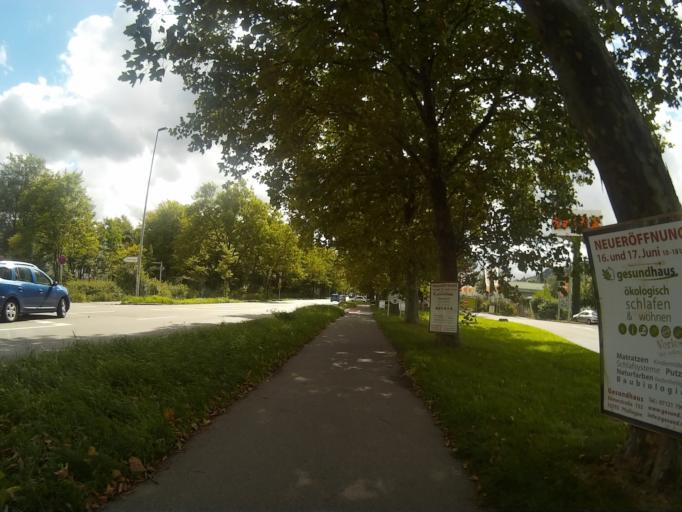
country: DE
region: Baden-Wuerttemberg
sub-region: Tuebingen Region
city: Pfullingen
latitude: 48.4824
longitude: 9.2237
